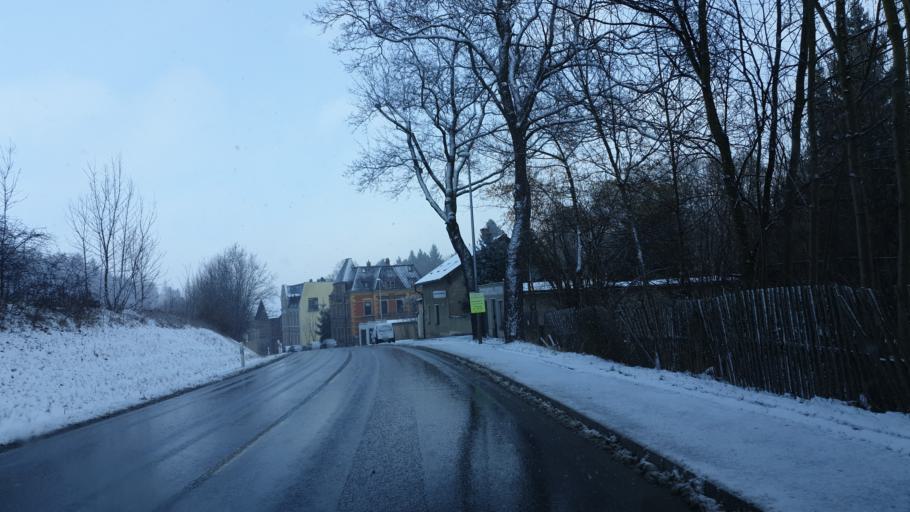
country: DE
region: Saxony
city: Oelsnitz
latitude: 50.4072
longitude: 12.1584
